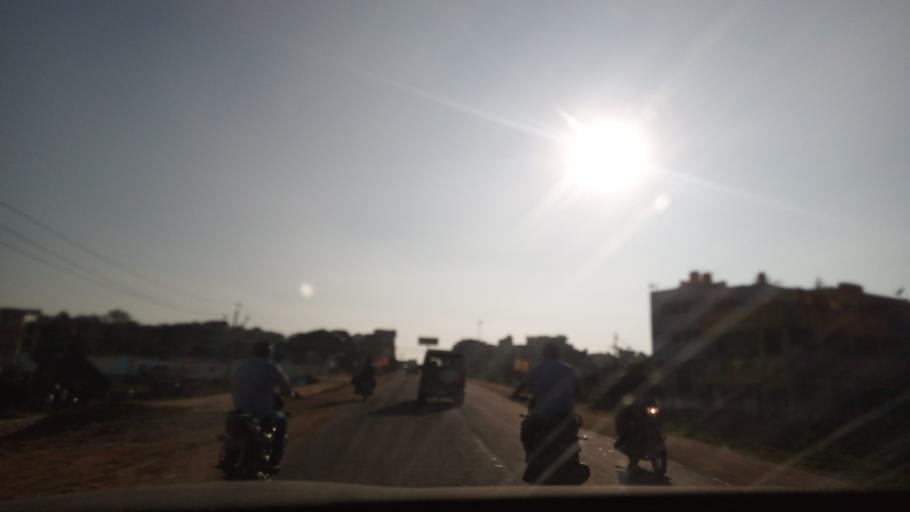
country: IN
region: Tamil Nadu
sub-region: Krishnagiri
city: Hosur
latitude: 12.7211
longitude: 77.8373
